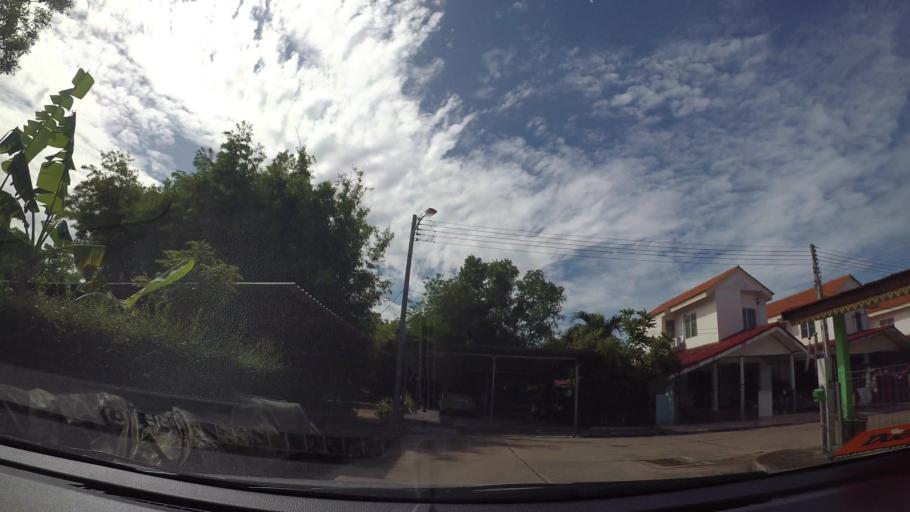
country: TH
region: Chon Buri
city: Sattahip
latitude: 12.6712
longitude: 100.9565
